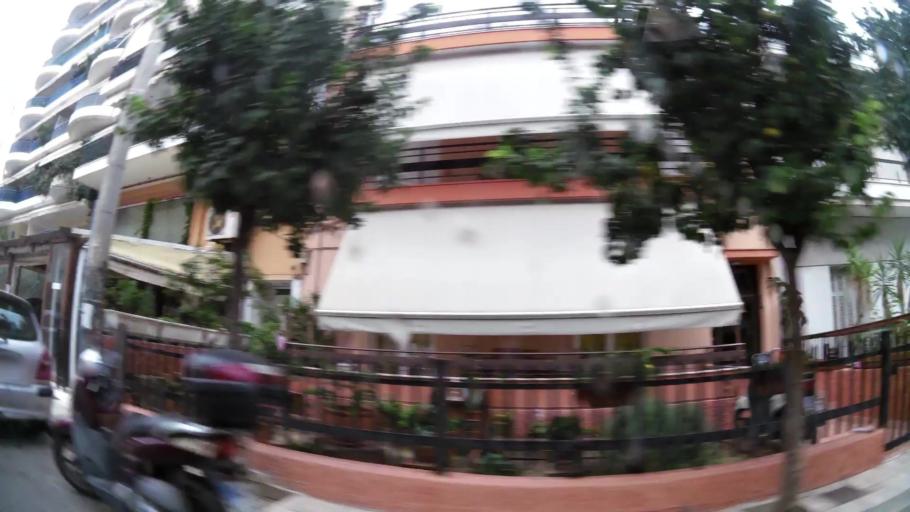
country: GR
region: Attica
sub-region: Nomos Piraios
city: Agios Ioannis Rentis
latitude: 37.9599
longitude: 23.6738
